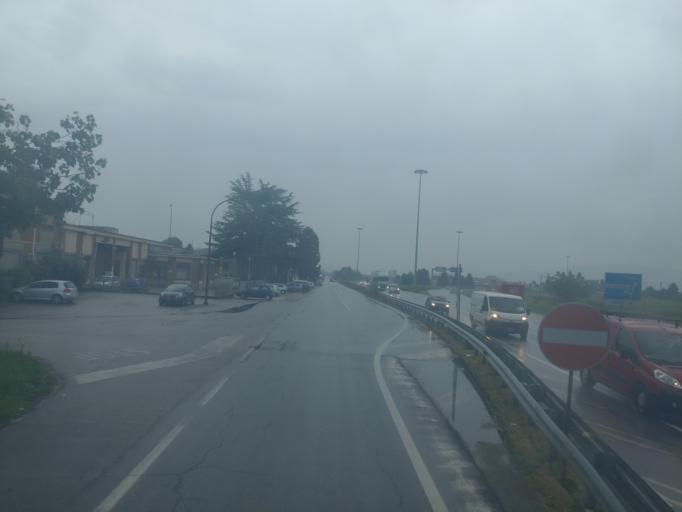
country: IT
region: Piedmont
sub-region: Provincia di Torino
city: La Loggia
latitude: 44.9387
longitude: 7.6708
